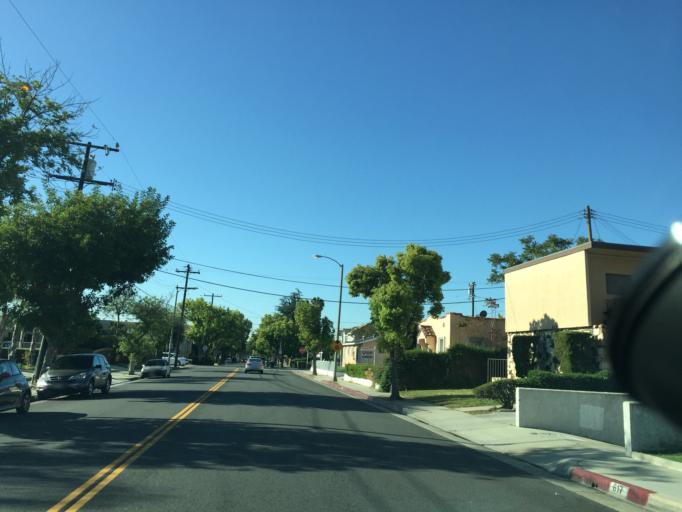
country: US
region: California
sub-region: Los Angeles County
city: Alhambra
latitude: 34.0902
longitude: -118.1197
